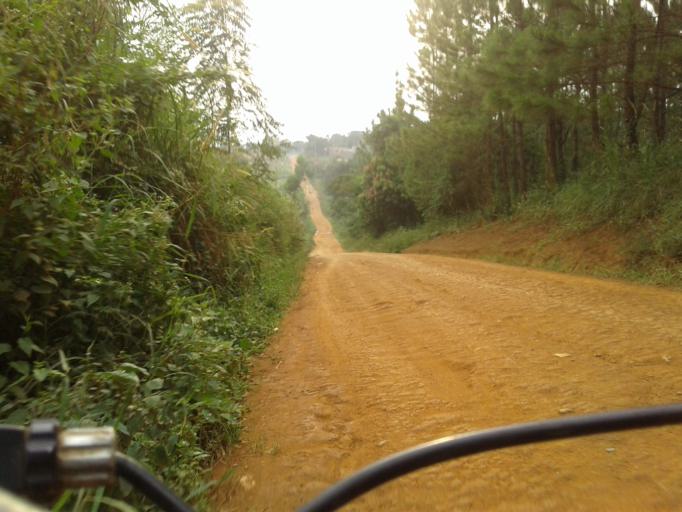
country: UG
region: Western Region
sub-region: Hoima District
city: Hoima
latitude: 1.4257
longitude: 31.3268
